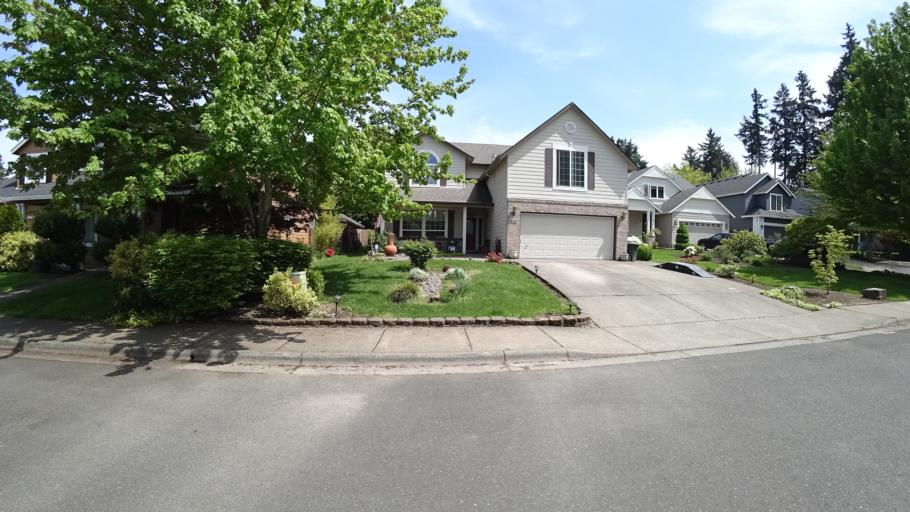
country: US
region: Oregon
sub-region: Washington County
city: Hillsboro
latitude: 45.5127
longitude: -122.9291
